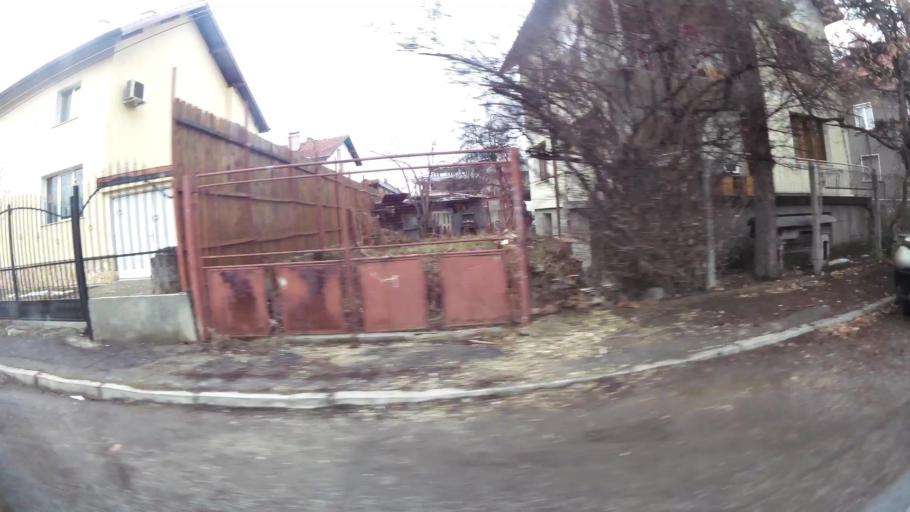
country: BG
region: Sofiya
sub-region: Obshtina Bozhurishte
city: Bozhurishte
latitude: 42.7411
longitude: 23.2663
